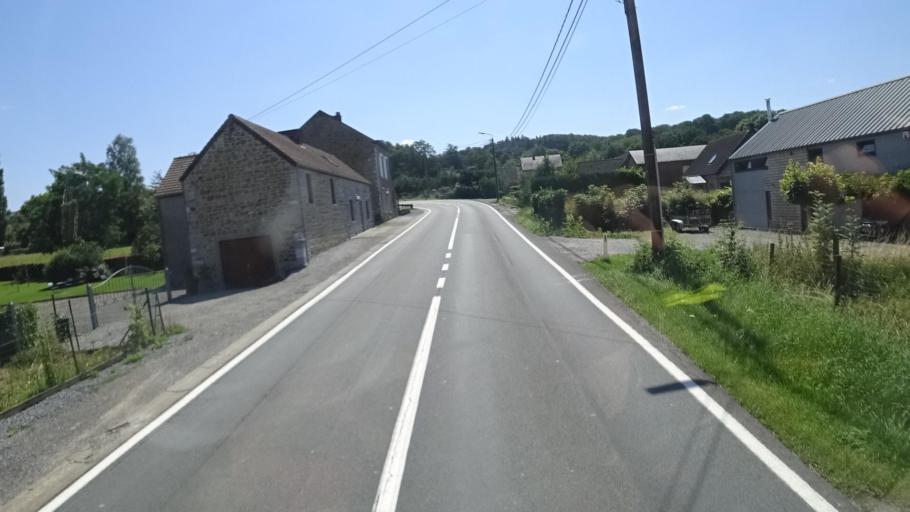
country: BE
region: Wallonia
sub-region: Province de Namur
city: Floreffe
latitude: 50.4187
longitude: 4.7752
